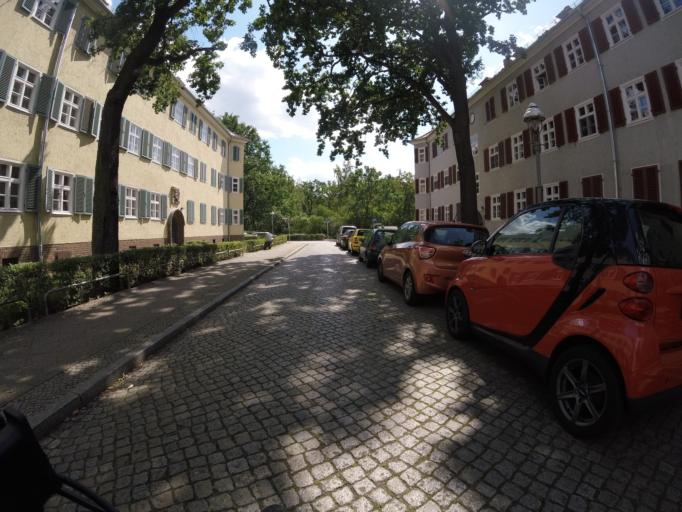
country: DE
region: Berlin
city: Siemensstadt
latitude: 52.5441
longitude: 13.2644
